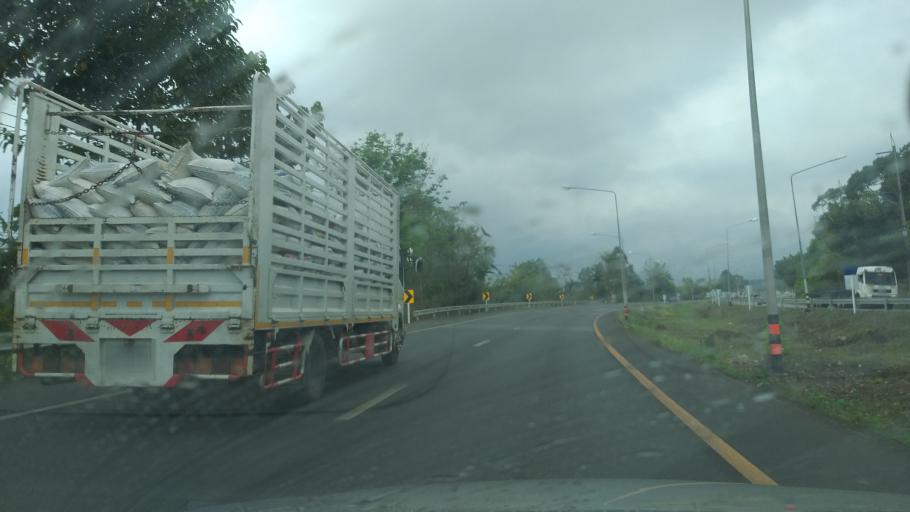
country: TH
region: Chanthaburi
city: Khlung
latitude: 12.4310
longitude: 102.3115
